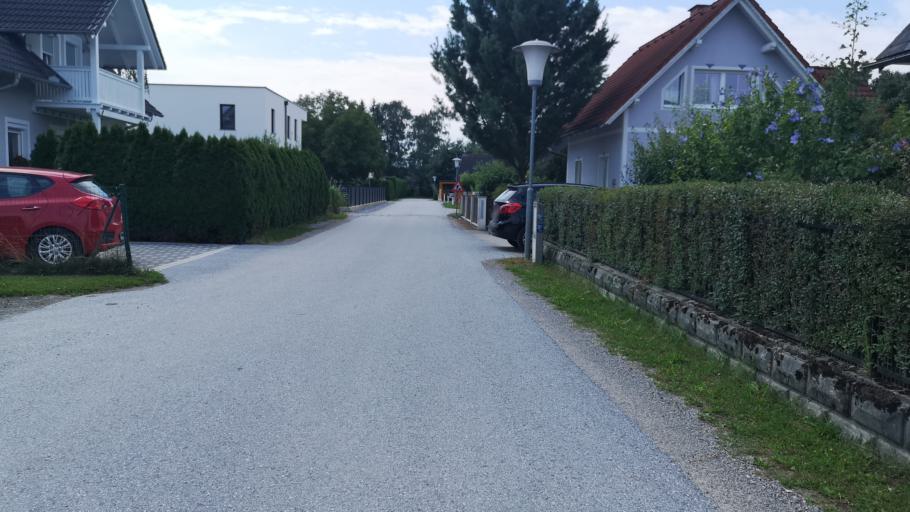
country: AT
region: Styria
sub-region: Politischer Bezirk Leibnitz
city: Weitendorf
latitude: 46.9017
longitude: 15.4767
